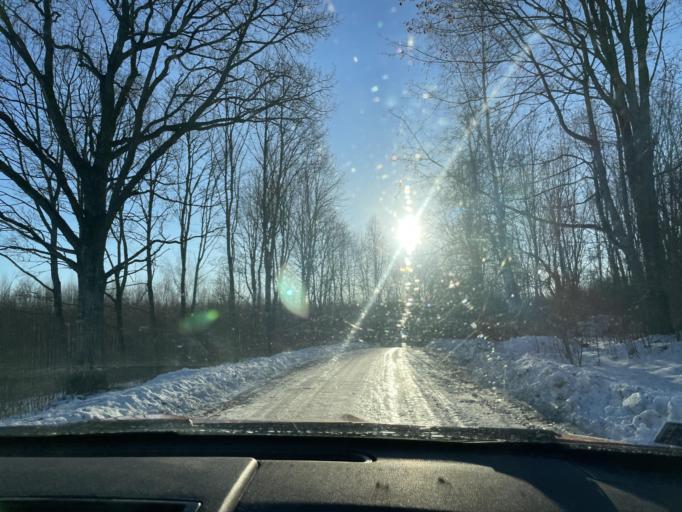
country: LV
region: Ludzas Rajons
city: Ludza
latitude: 56.4539
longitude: 27.6361
